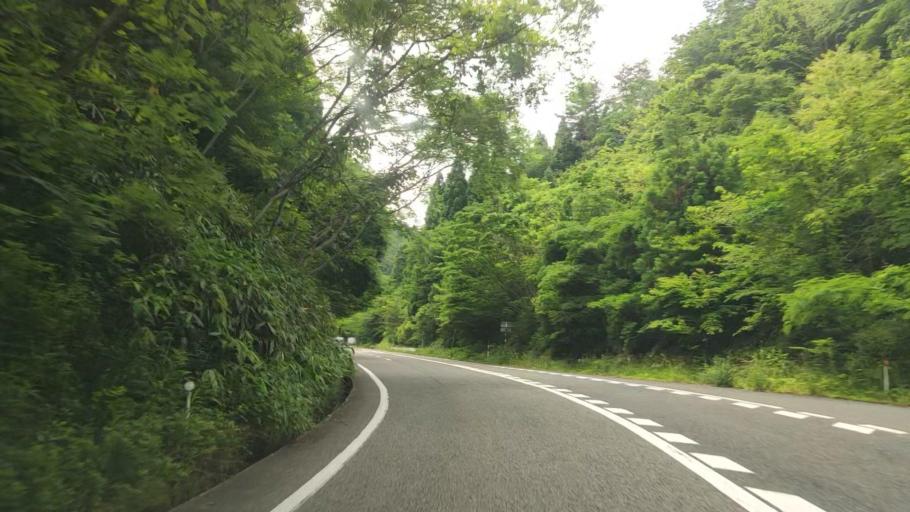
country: JP
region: Tottori
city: Yonago
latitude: 35.2725
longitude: 133.4324
